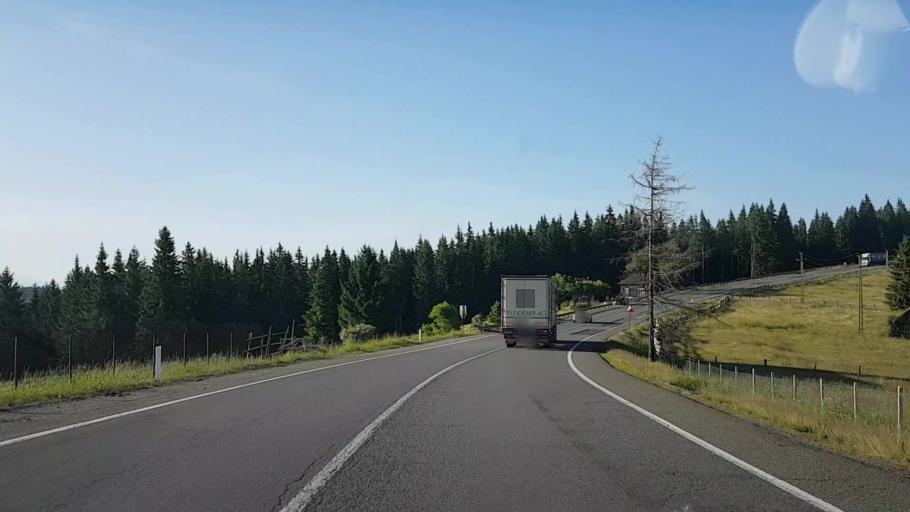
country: RO
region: Bistrita-Nasaud
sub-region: Comuna Lunca Ilvei
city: Lunca Ilvei
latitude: 47.2770
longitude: 25.0283
